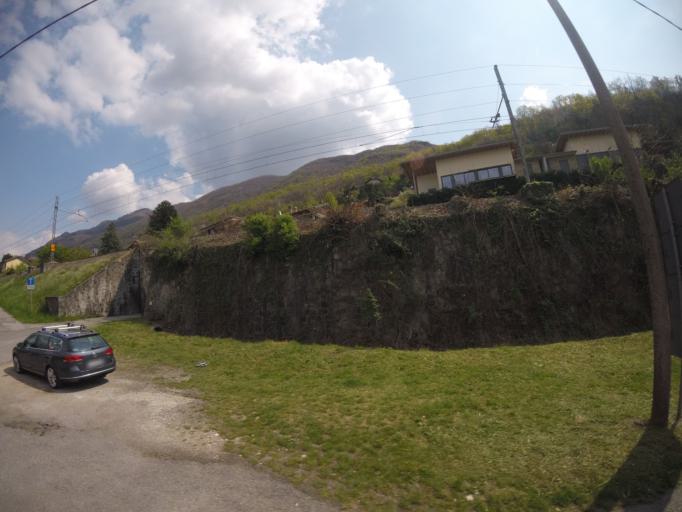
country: IT
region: Piedmont
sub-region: Provincia Verbano-Cusio-Ossola
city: Omegna
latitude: 45.8546
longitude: 8.4074
